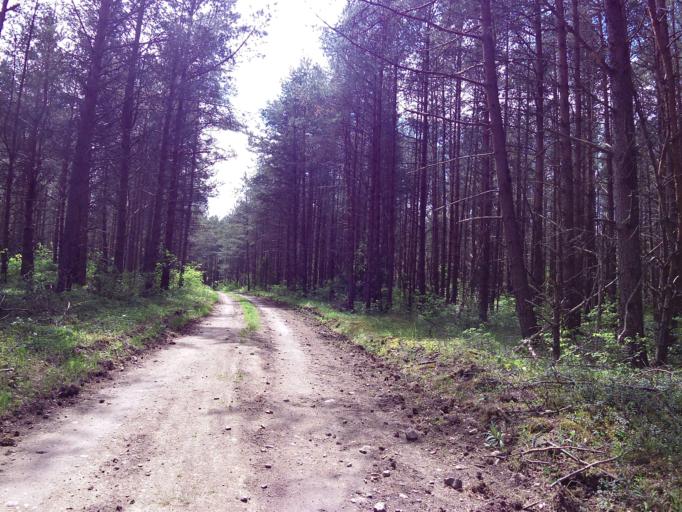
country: EE
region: Harju
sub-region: Paldiski linn
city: Paldiski
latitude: 59.2609
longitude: 23.7454
